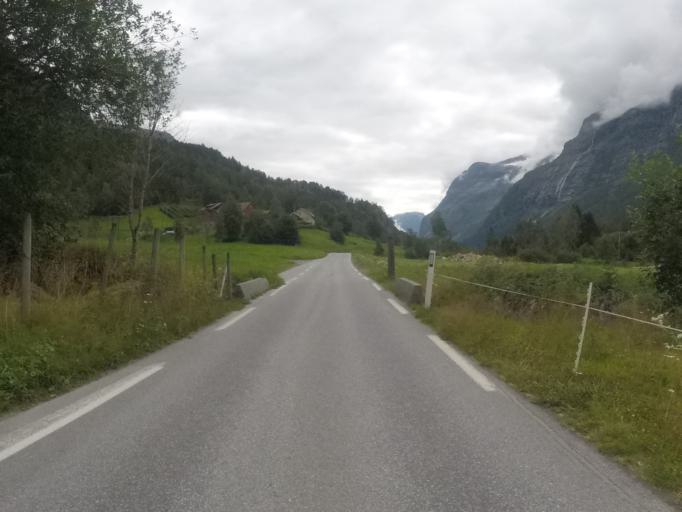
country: NO
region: Sogn og Fjordane
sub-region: Stryn
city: Stryn
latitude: 61.8660
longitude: 6.8830
